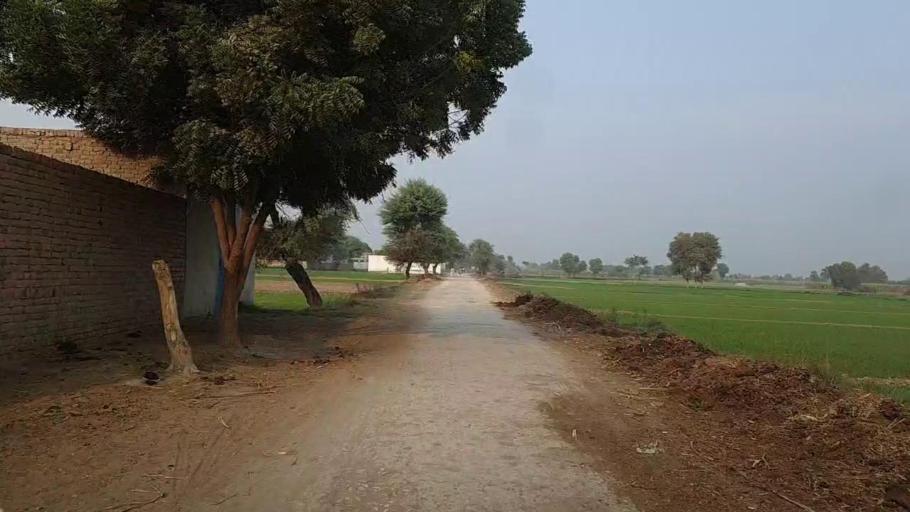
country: PK
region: Sindh
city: Setharja Old
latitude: 27.0908
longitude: 68.4978
